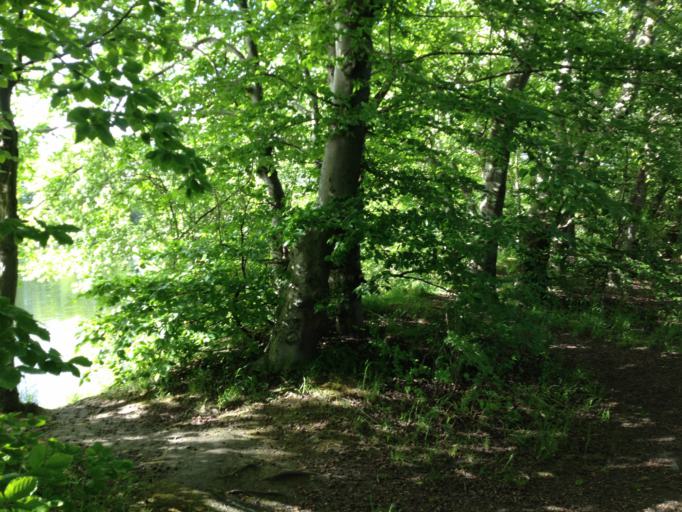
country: DK
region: Capital Region
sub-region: Fredensborg Kommune
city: Niva
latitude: 55.9323
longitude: 12.5192
